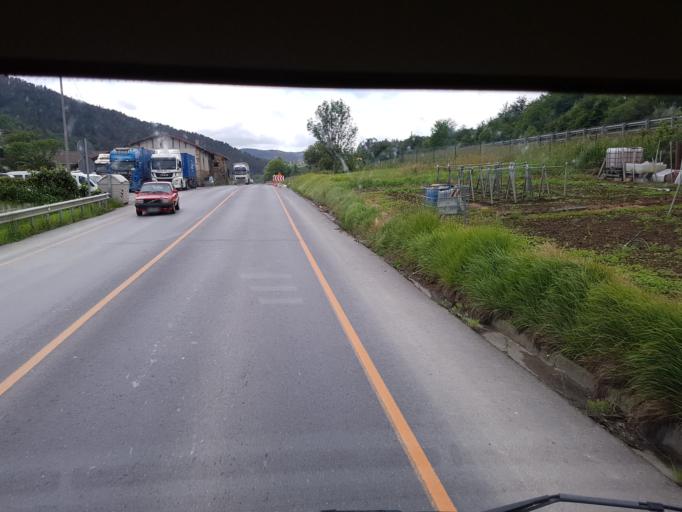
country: ES
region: Basque Country
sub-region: Bizkaia
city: Iurreta
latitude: 43.1872
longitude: -2.6778
